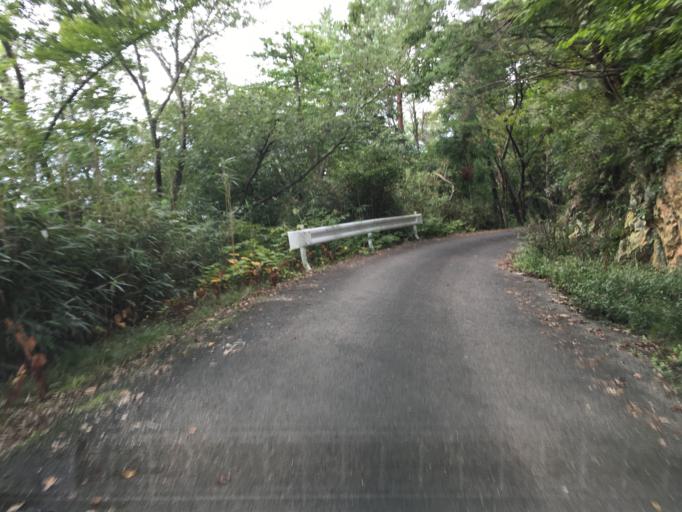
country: JP
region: Fukushima
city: Fukushima-shi
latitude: 37.7735
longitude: 140.4700
